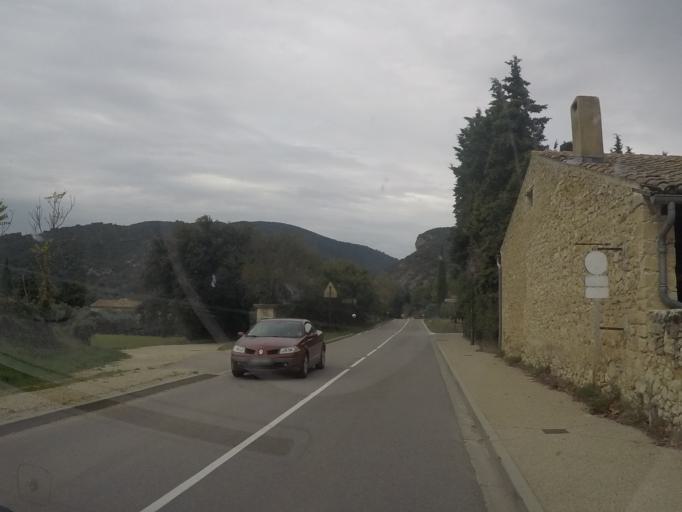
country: FR
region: Provence-Alpes-Cote d'Azur
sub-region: Departement du Vaucluse
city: Lourmarin
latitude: 43.7692
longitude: 5.3588
